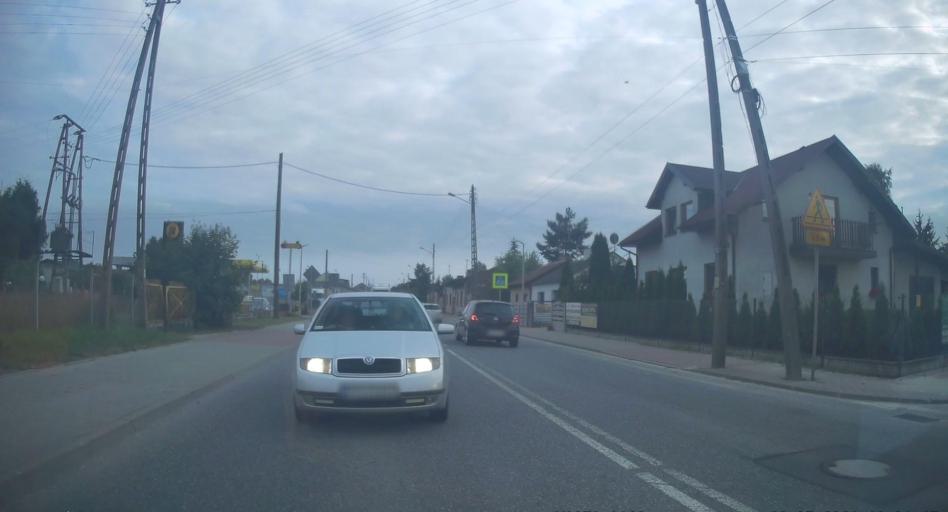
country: PL
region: Lodz Voivodeship
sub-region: Powiat radomszczanski
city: Kamiensk
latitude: 51.1958
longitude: 19.4989
